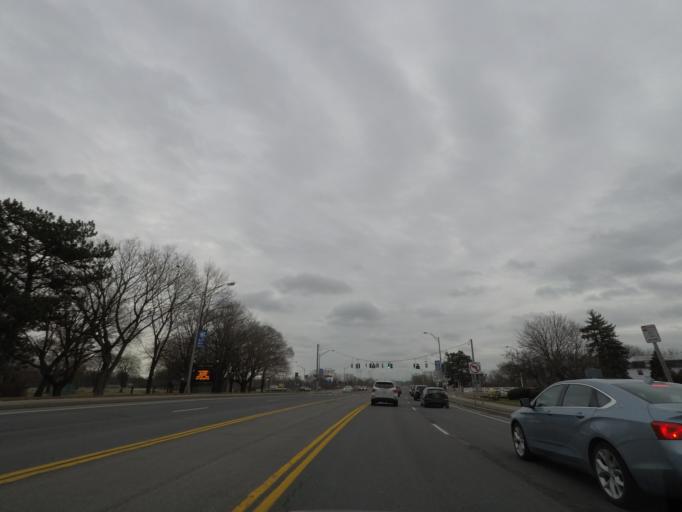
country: US
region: New York
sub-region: Schenectady County
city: Scotia
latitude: 42.8236
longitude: -73.9591
